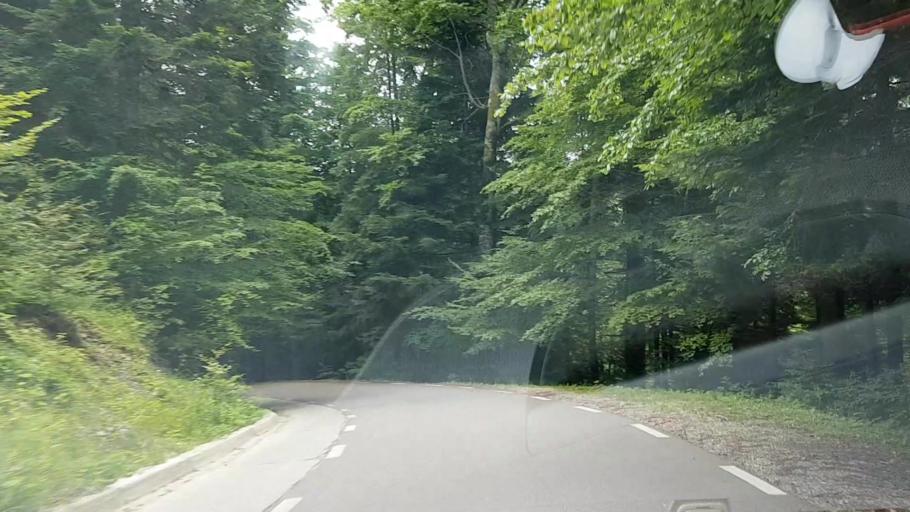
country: RO
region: Suceava
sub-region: Comuna Crucea
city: Crucea
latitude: 47.4330
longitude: 25.5737
